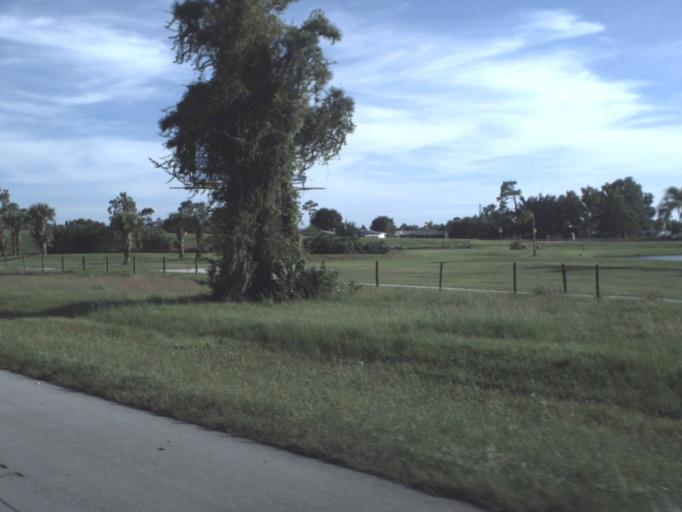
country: US
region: Florida
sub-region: Charlotte County
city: Charlotte Park
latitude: 26.8866
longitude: -81.9934
